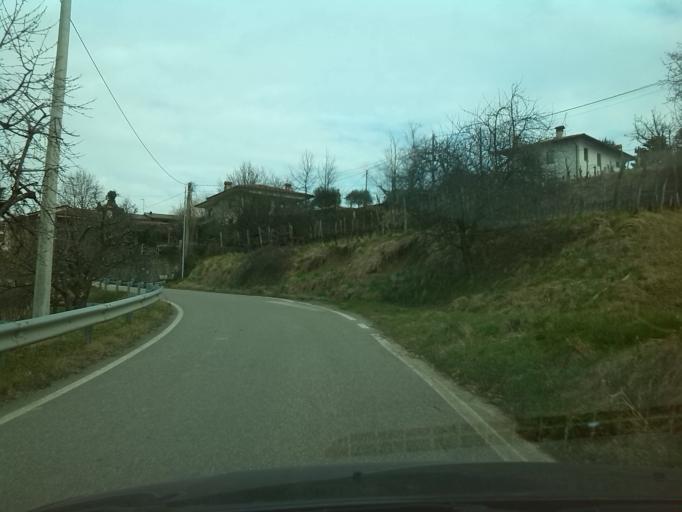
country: IT
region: Friuli Venezia Giulia
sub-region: Provincia di Gorizia
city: San Floriano del Collio
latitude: 45.9675
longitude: 13.5755
